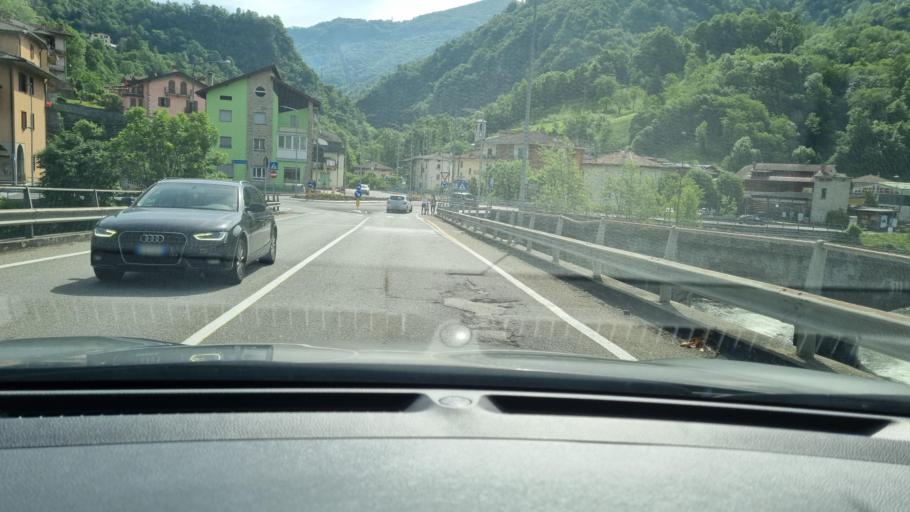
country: IT
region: Lombardy
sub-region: Provincia di Bergamo
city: Zogno
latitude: 45.8079
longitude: 9.6796
